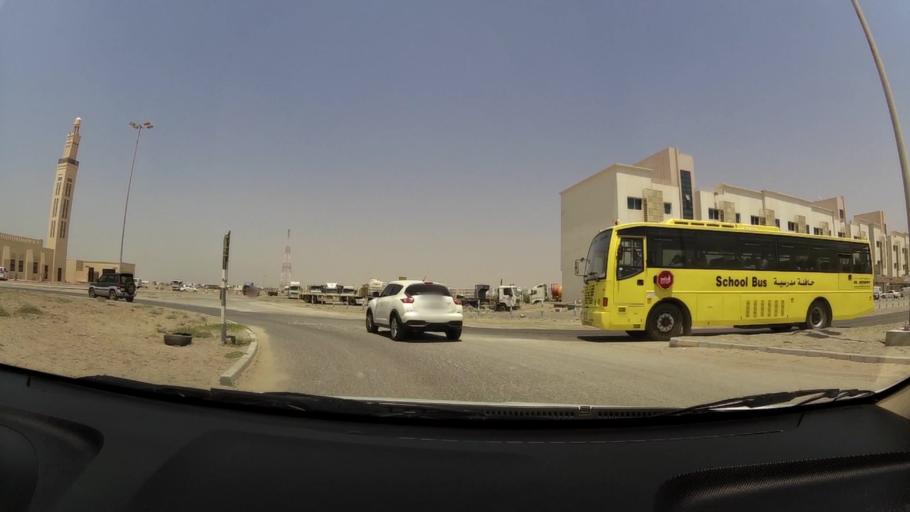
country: AE
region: Umm al Qaywayn
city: Umm al Qaywayn
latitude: 25.5123
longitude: 55.5575
